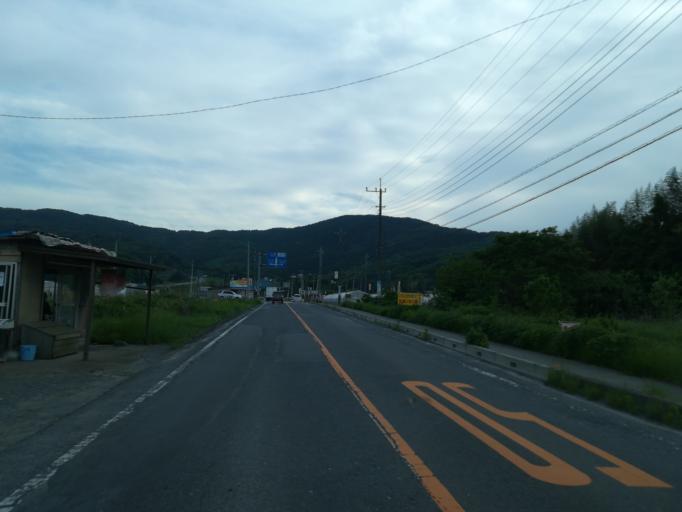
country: JP
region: Ibaraki
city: Tsukuba
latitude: 36.1892
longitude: 140.1714
